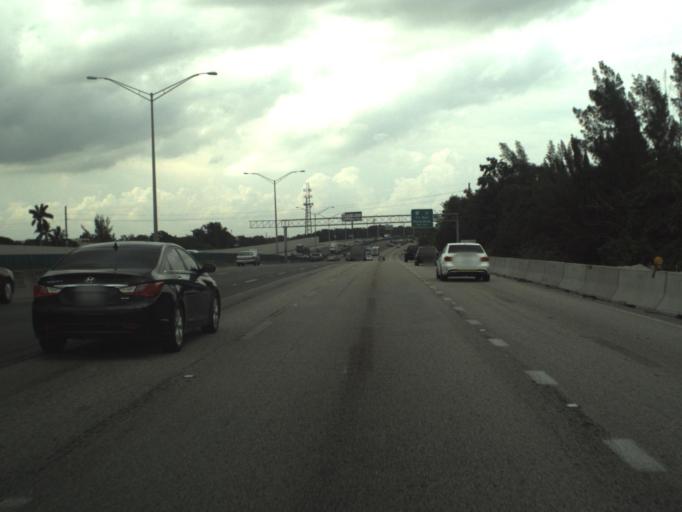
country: US
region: Florida
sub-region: Broward County
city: Hollywood
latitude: 26.0190
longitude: -80.1671
